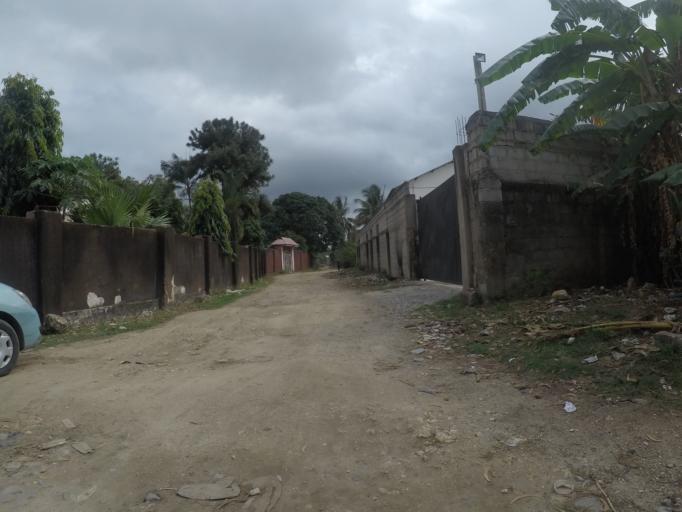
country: TZ
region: Zanzibar Urban/West
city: Zanzibar
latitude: -6.2146
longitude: 39.2197
